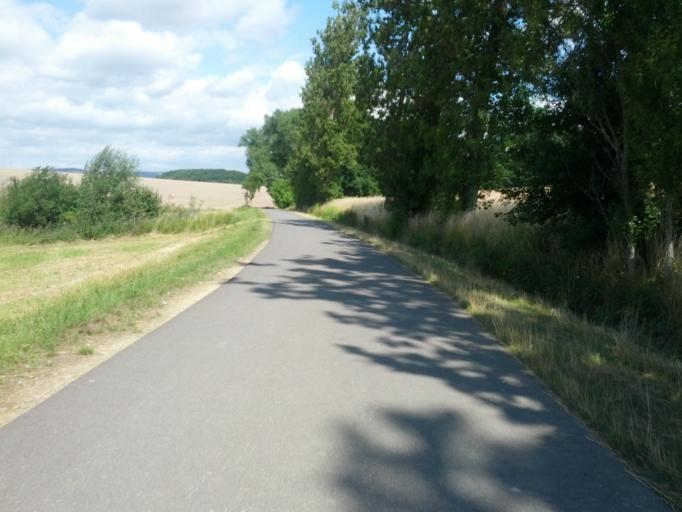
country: DE
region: Thuringia
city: Krauthausen
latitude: 51.0095
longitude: 10.2735
